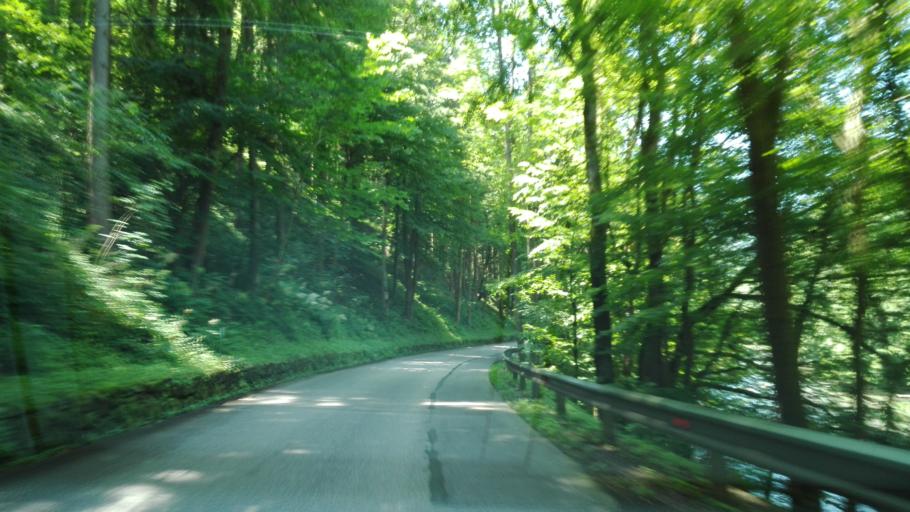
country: AT
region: Upper Austria
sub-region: Politischer Bezirk Rohrbach
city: Kleinzell im Muehlkreis
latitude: 48.3816
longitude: 13.9297
